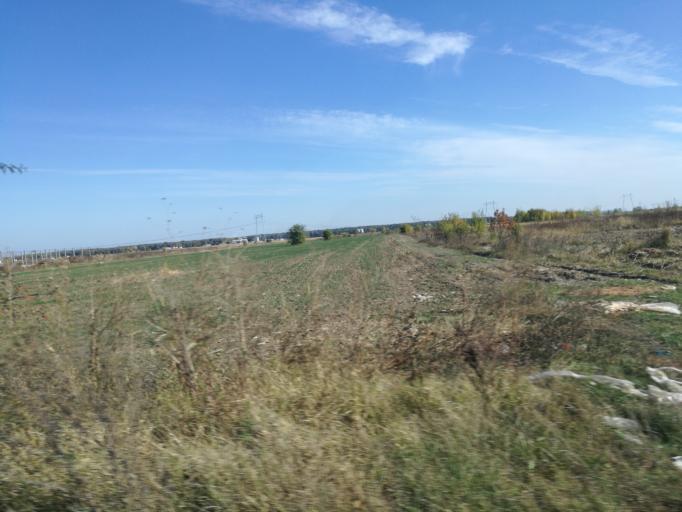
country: RO
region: Giurgiu
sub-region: Comuna Joita
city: Bacu
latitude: 44.4671
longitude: 25.8833
